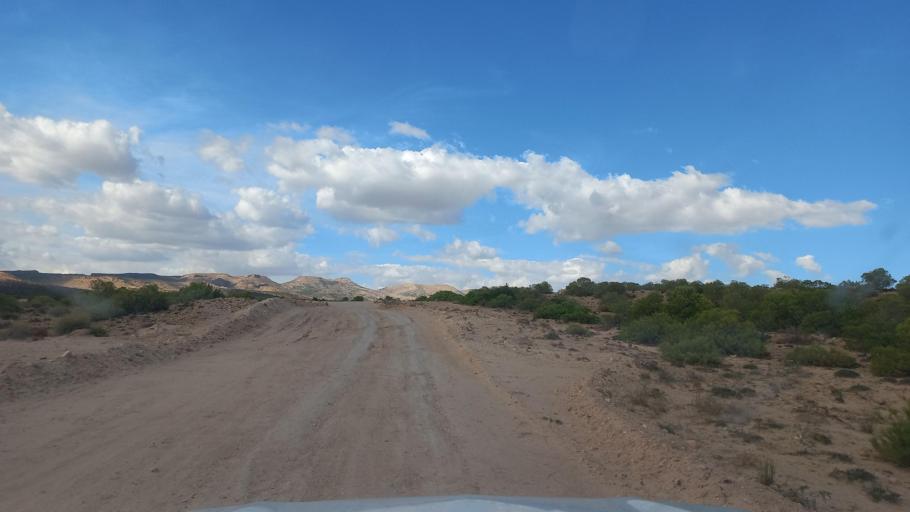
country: TN
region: Al Qasrayn
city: Sbiba
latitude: 35.3984
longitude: 9.0113
